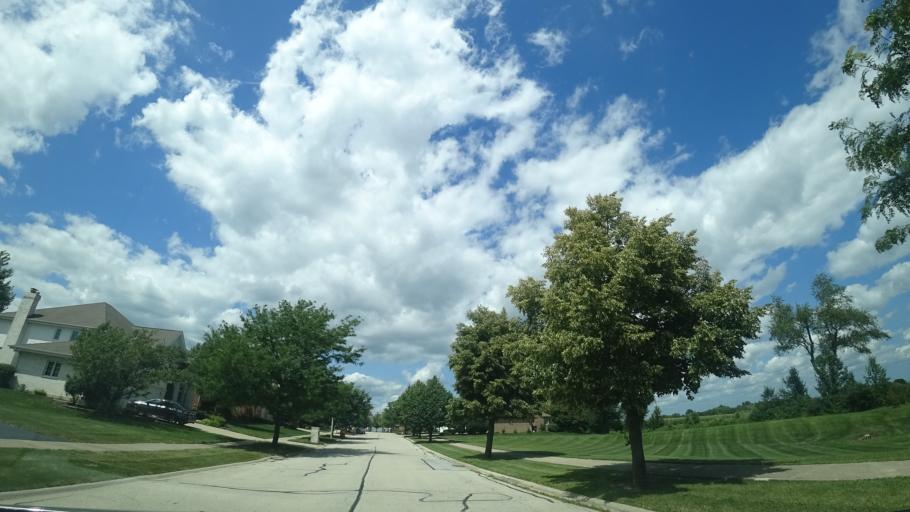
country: US
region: Illinois
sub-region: Will County
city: Homer Glen
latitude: 41.5801
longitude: -87.8962
